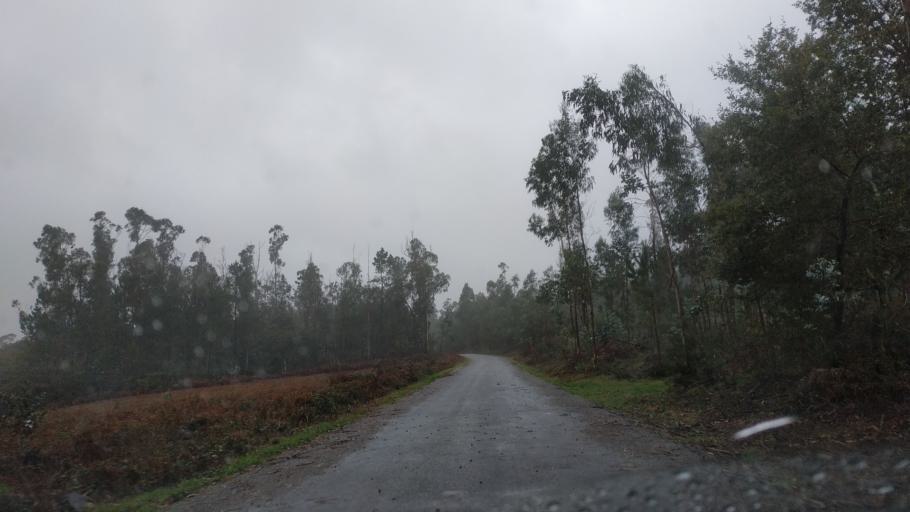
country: ES
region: Galicia
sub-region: Provincia da Coruna
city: Negreira
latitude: 42.9108
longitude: -8.7676
